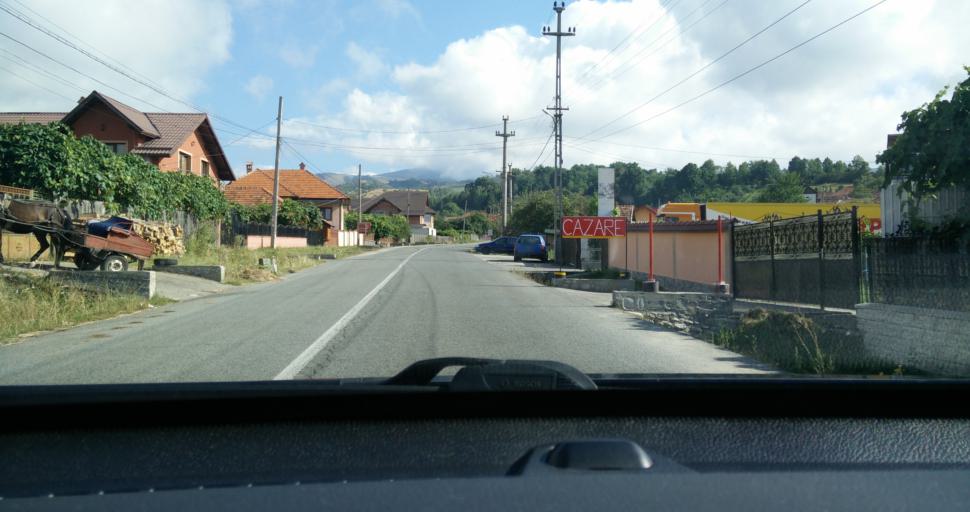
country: RO
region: Gorj
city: Novaci-Straini
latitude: 45.1799
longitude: 23.6764
